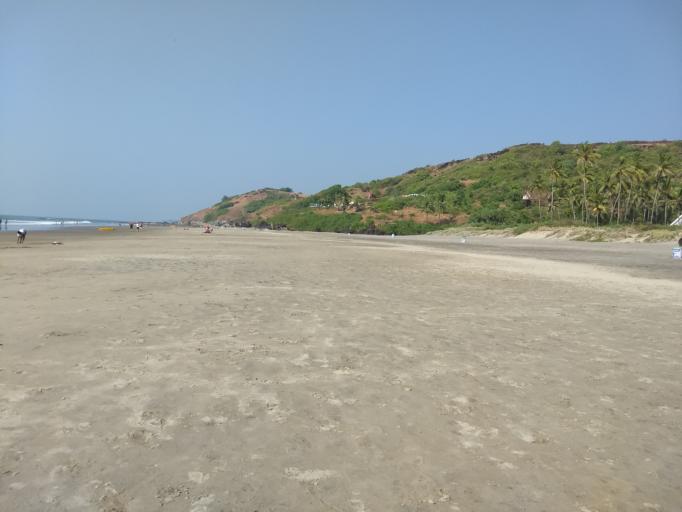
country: IN
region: Goa
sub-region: North Goa
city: Vagator
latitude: 15.6022
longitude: 73.7337
